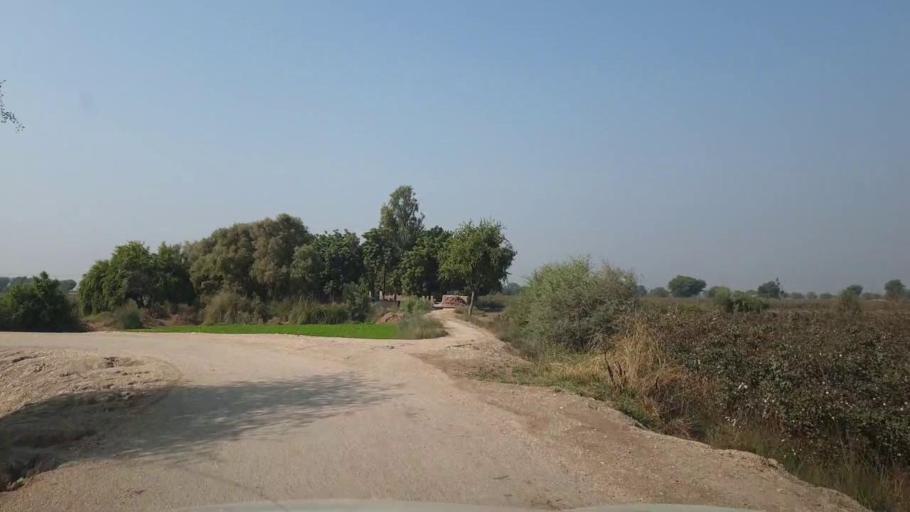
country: PK
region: Sindh
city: Bhan
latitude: 26.5017
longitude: 67.7906
